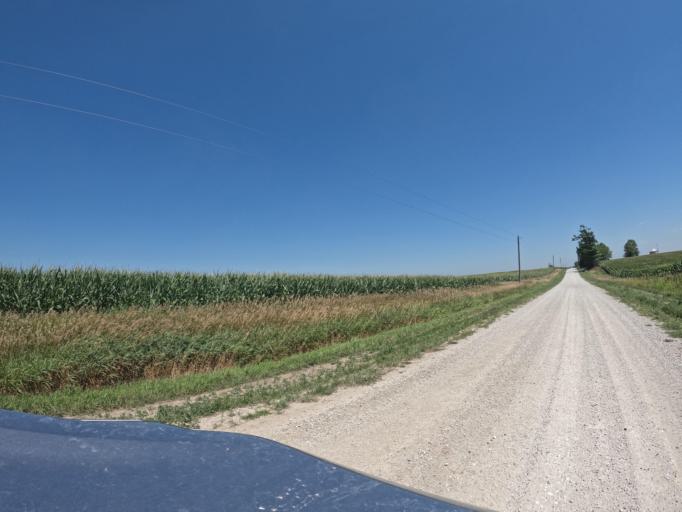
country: US
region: Iowa
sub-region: Keokuk County
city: Sigourney
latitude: 41.4235
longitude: -92.3350
